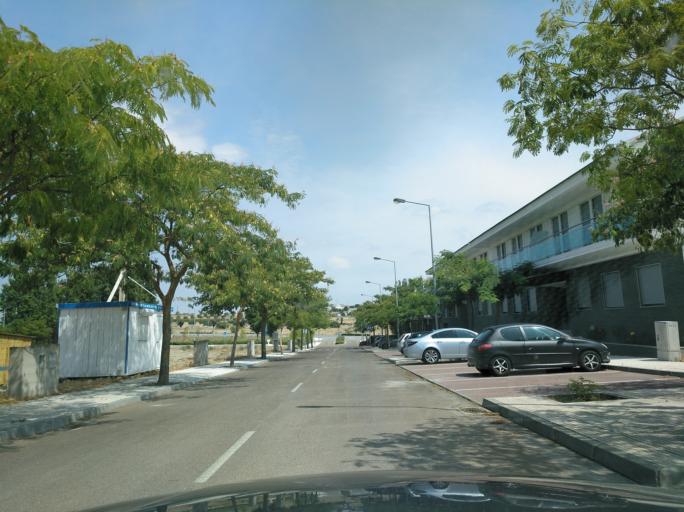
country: PT
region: Portalegre
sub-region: Campo Maior
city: Campo Maior
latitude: 39.0159
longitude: -7.0760
